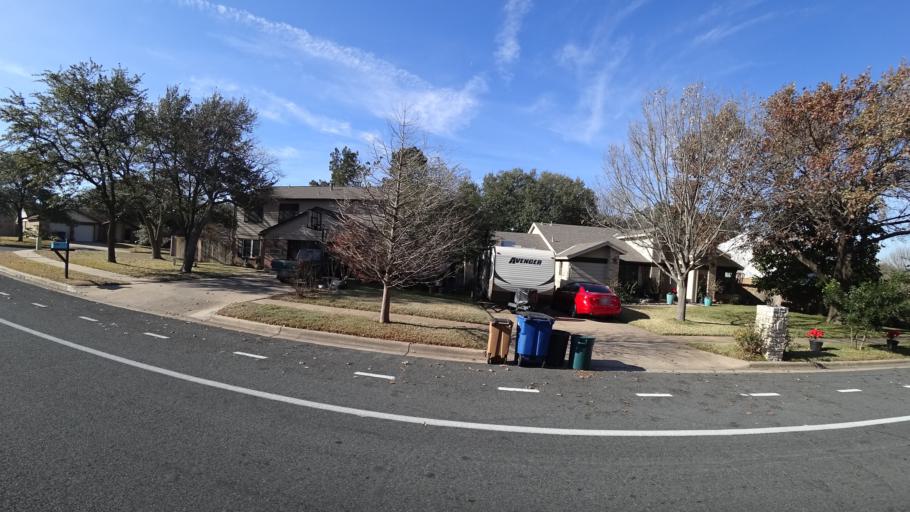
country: US
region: Texas
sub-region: Travis County
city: Wells Branch
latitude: 30.3892
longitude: -97.6946
